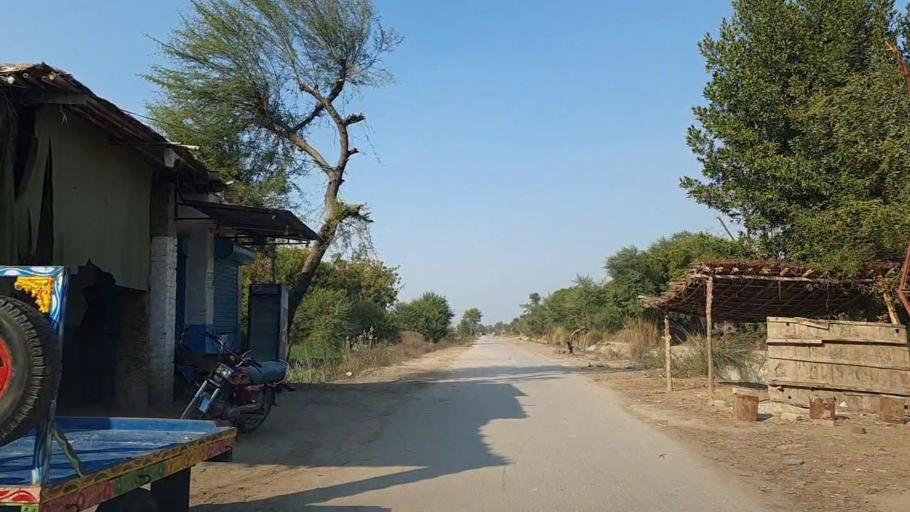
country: PK
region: Sindh
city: Daur
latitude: 26.4045
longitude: 68.2591
